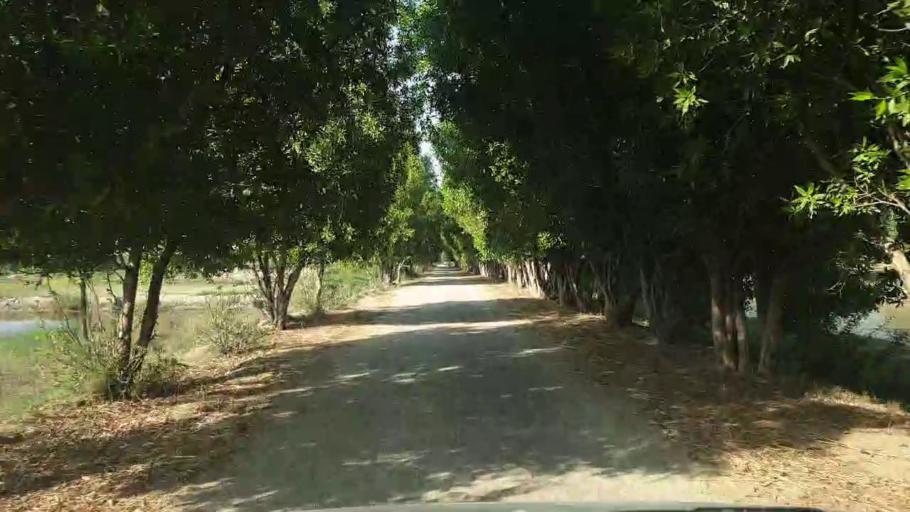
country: PK
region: Sindh
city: Badin
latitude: 24.6245
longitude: 68.8148
